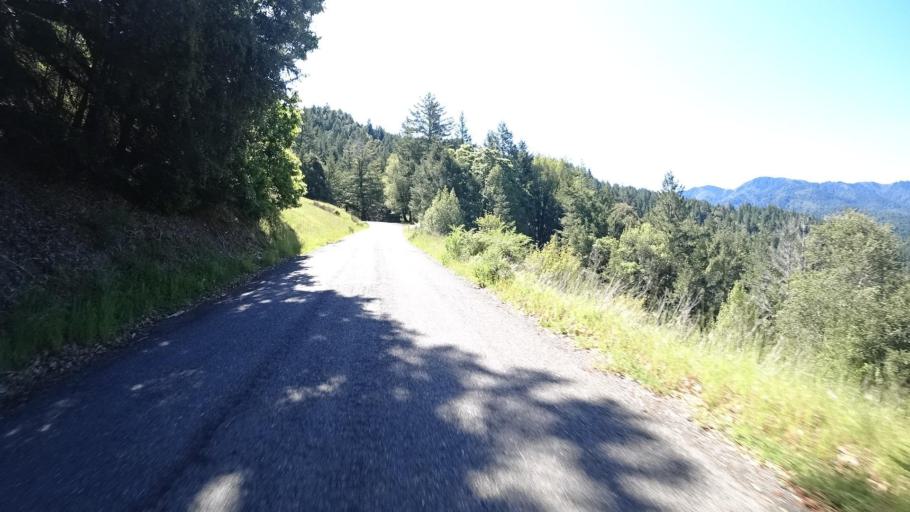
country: US
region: California
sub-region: Humboldt County
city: Rio Dell
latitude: 40.2178
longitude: -124.1123
